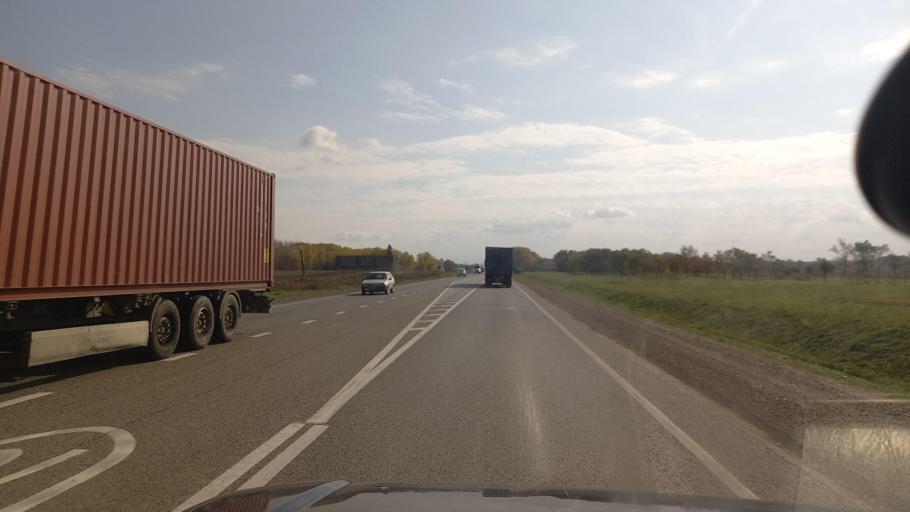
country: RU
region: Krasnodarskiy
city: Novoukrainskiy
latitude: 44.8886
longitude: 38.0773
